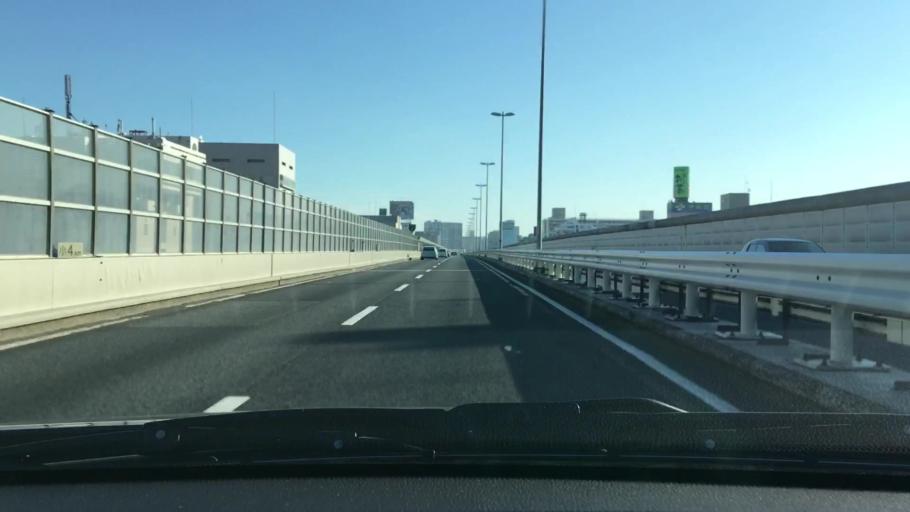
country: JP
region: Tokyo
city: Urayasu
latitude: 35.6940
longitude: 139.8329
